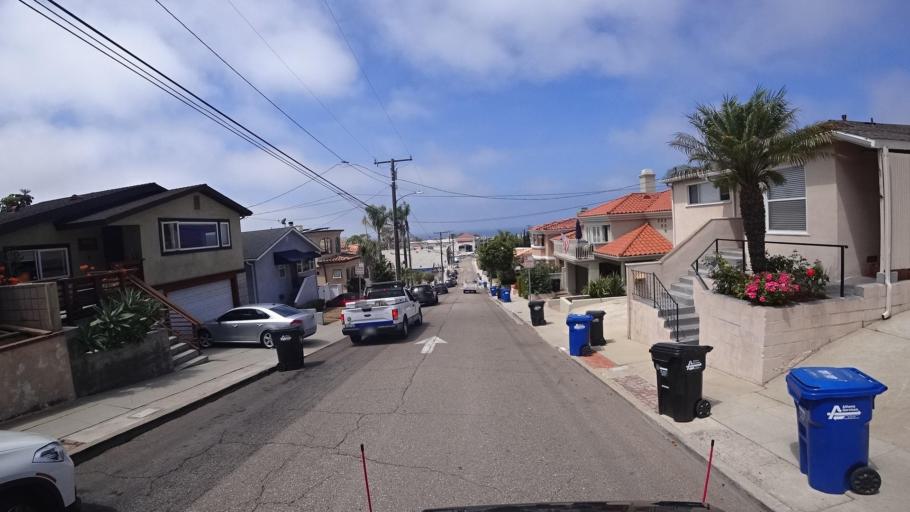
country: US
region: California
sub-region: Los Angeles County
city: Redondo Beach
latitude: 33.8568
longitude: -118.3888
